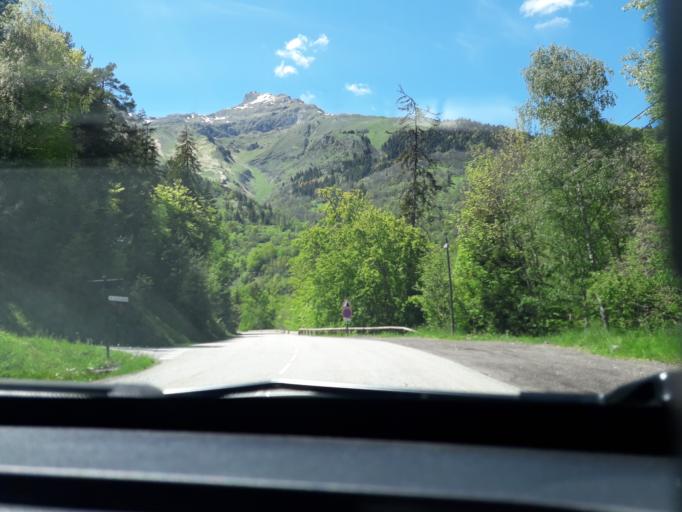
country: FR
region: Rhone-Alpes
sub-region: Departement de la Savoie
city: Saint-Martin-de-Belleville
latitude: 45.4219
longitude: 6.4854
